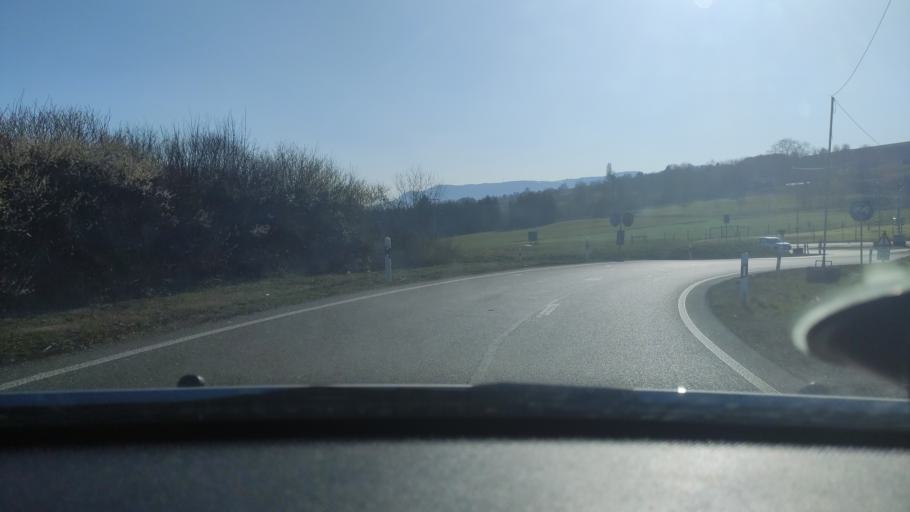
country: DE
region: Baden-Wuerttemberg
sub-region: Tuebingen Region
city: Grosselfingen
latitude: 48.3113
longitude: 8.8853
